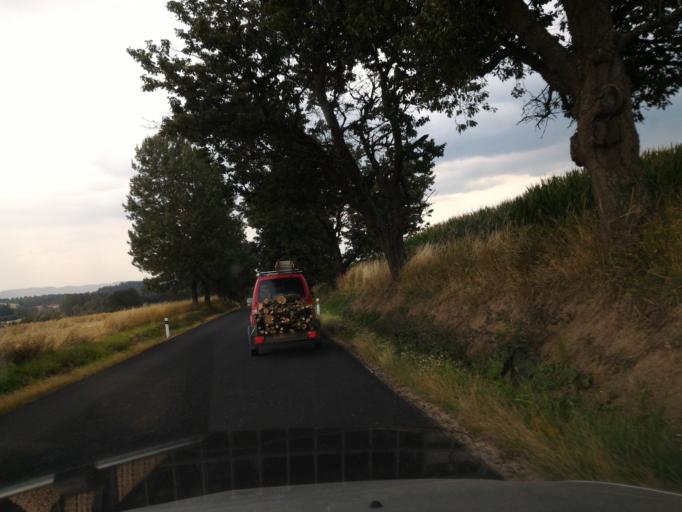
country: CZ
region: Vysocina
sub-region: Okres Jihlava
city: Telc
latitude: 49.2179
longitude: 15.4241
